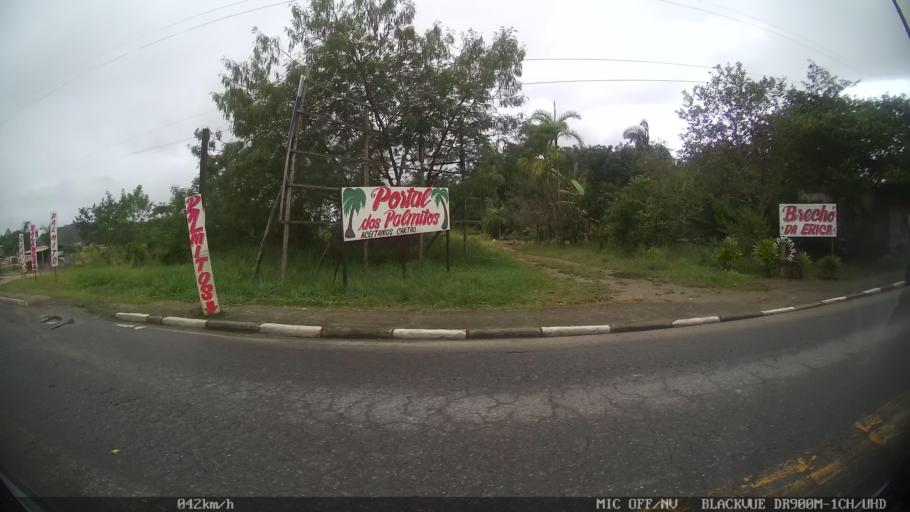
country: BR
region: Sao Paulo
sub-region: Juquia
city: Juquia
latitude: -24.3280
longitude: -47.6314
